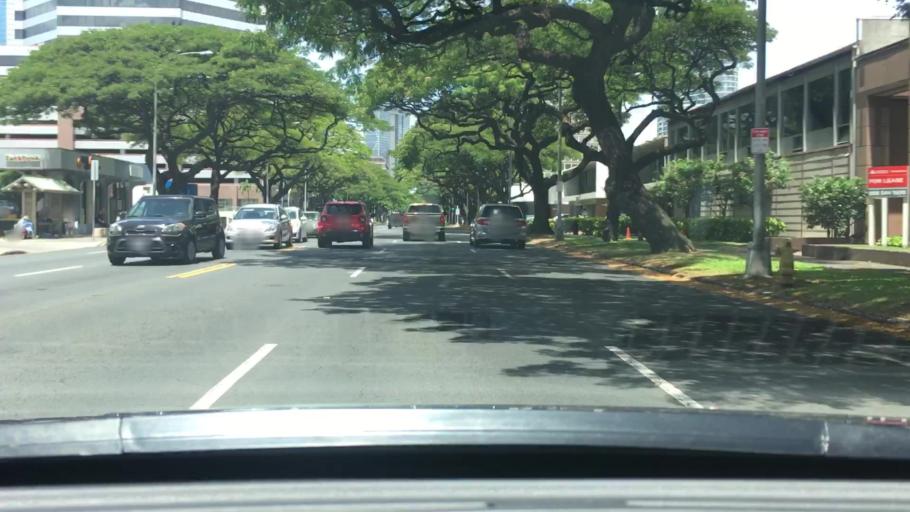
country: US
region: Hawaii
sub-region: Honolulu County
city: Honolulu
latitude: 21.2933
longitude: -157.8428
